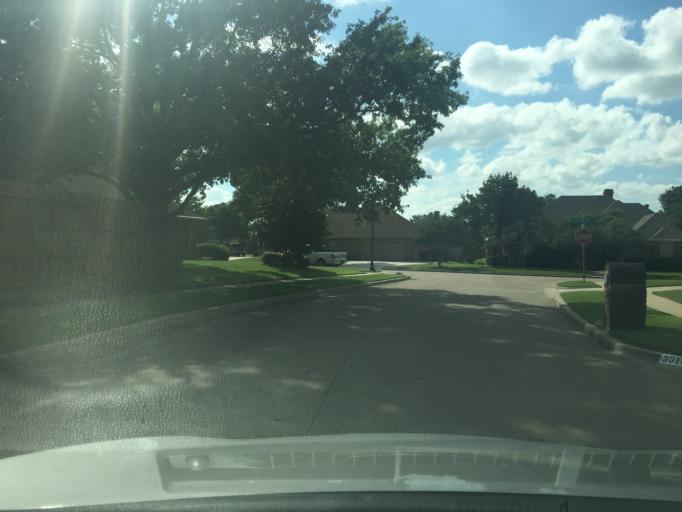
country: US
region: Texas
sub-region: Dallas County
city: Garland
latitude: 32.9357
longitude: -96.6753
